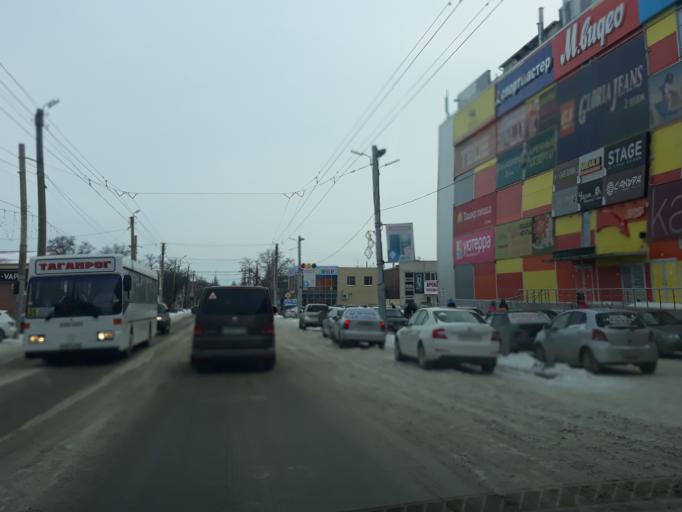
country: RU
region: Rostov
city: Taganrog
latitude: 47.2179
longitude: 38.8994
